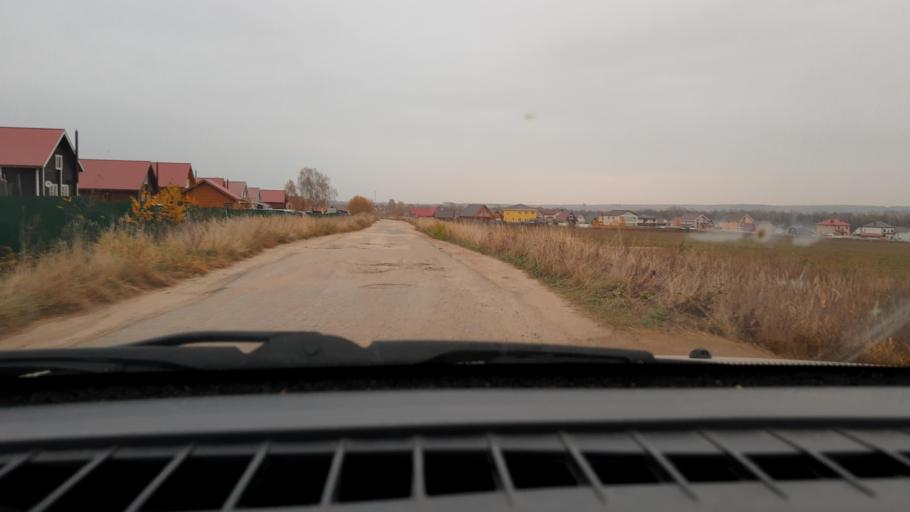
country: RU
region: Nizjnij Novgorod
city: Burevestnik
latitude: 56.0423
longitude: 43.8379
